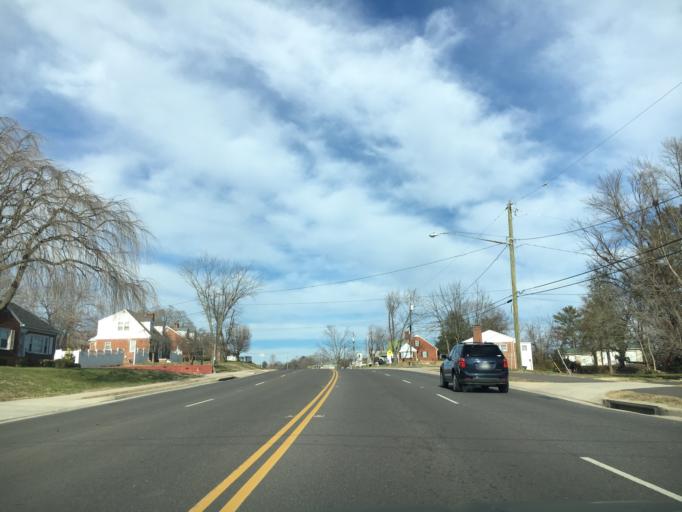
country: US
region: Virginia
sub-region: Culpeper County
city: Culpeper
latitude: 38.4829
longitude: -77.9926
